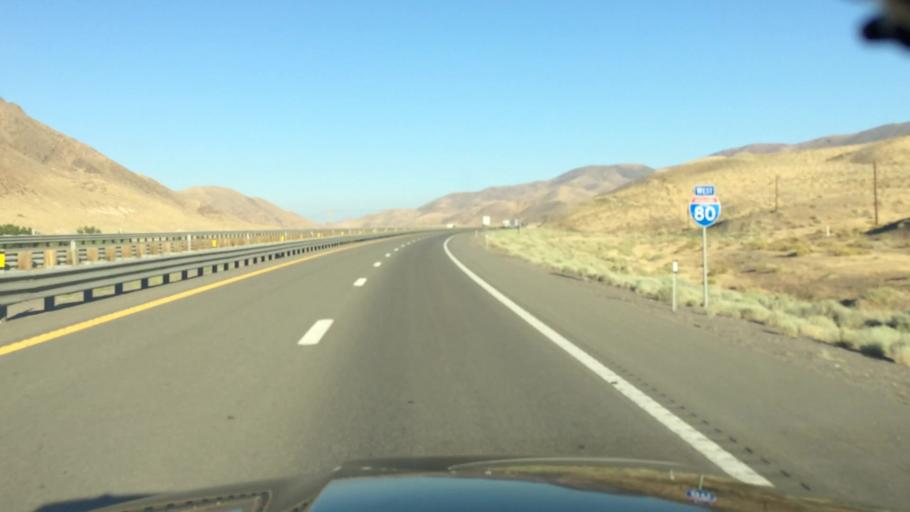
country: US
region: Nevada
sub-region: Lyon County
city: Fernley
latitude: 39.5892
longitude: -119.3959
